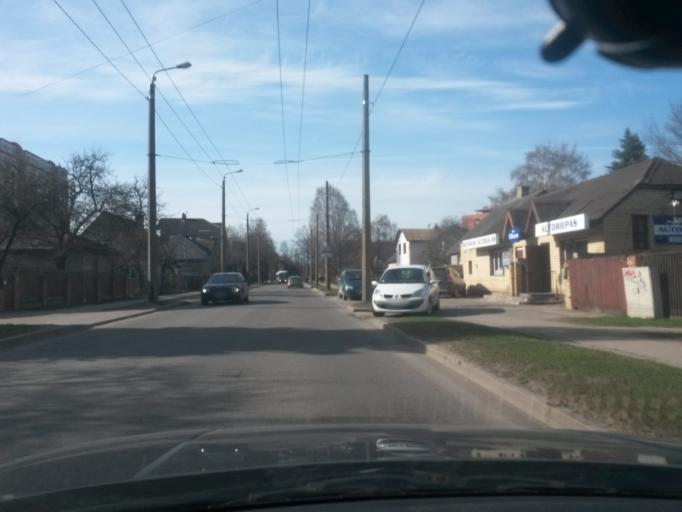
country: LV
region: Kekava
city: Balozi
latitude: 56.9078
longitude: 24.1982
